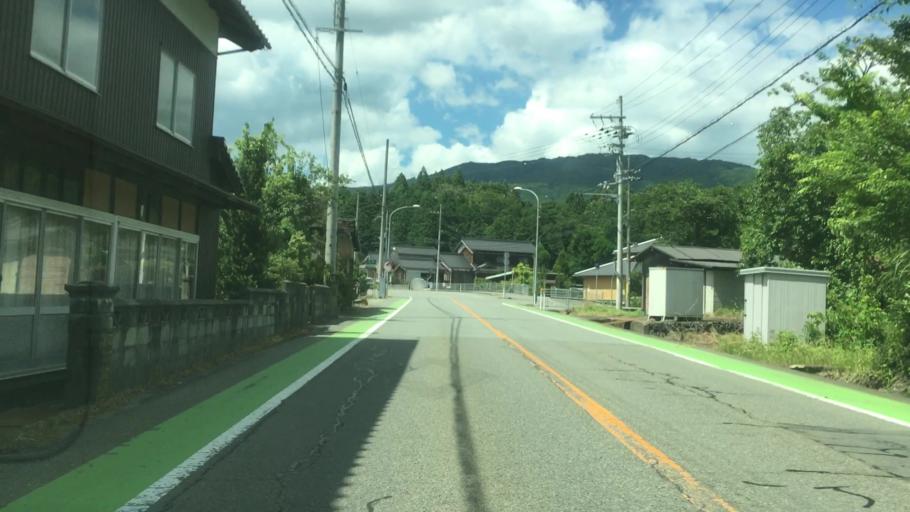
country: JP
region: Hyogo
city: Toyooka
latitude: 35.4798
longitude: 134.7086
